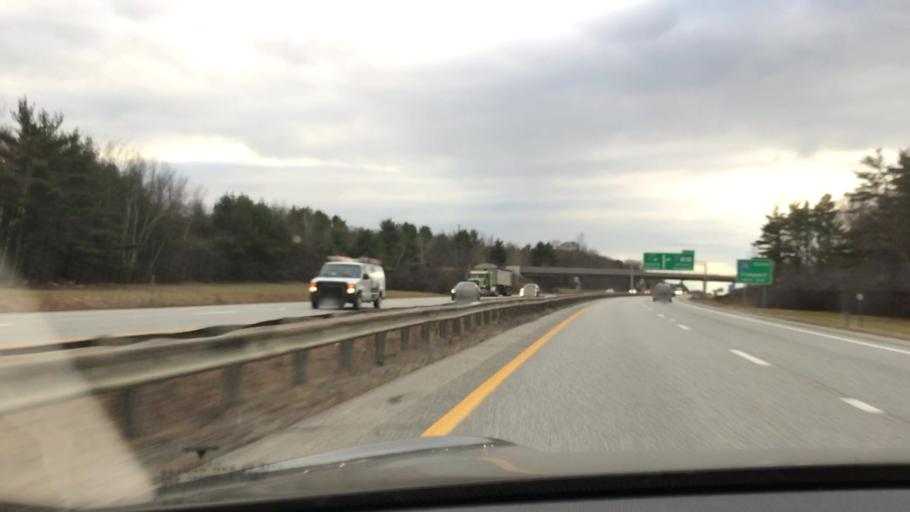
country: US
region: Maine
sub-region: Kennebec County
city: Gardiner
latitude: 44.2329
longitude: -69.8101
